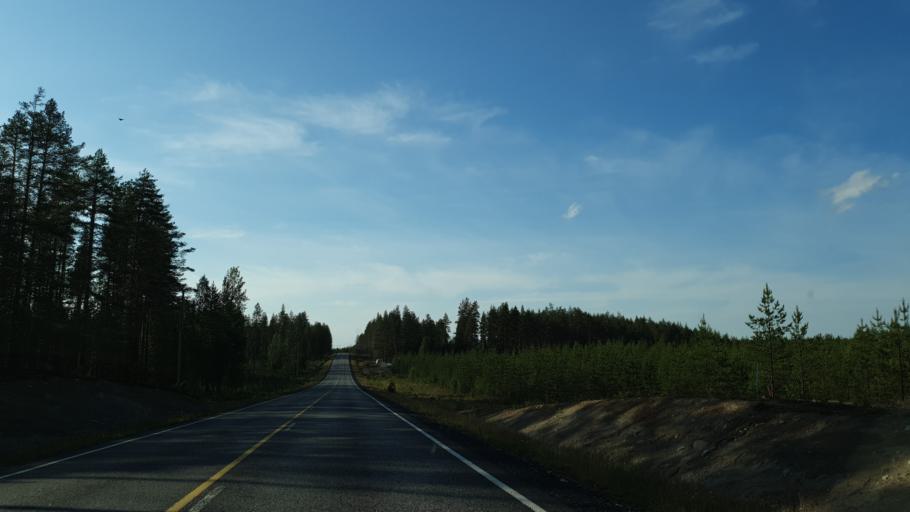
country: FI
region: Kainuu
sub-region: Kehys-Kainuu
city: Kuhmo
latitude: 64.0928
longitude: 29.4796
